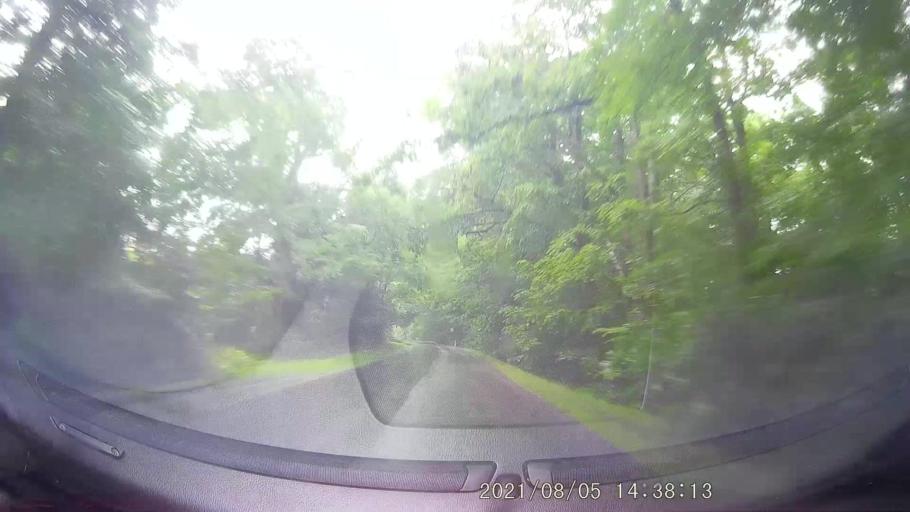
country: PL
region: Opole Voivodeship
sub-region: Powiat nyski
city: Sidzina
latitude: 50.4717
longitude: 17.4636
